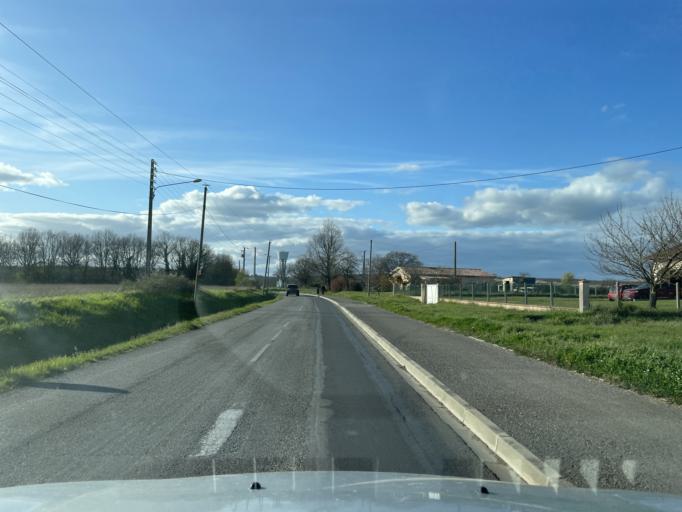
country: FR
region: Midi-Pyrenees
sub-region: Departement de la Haute-Garonne
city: Leguevin
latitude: 43.6048
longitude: 1.2225
